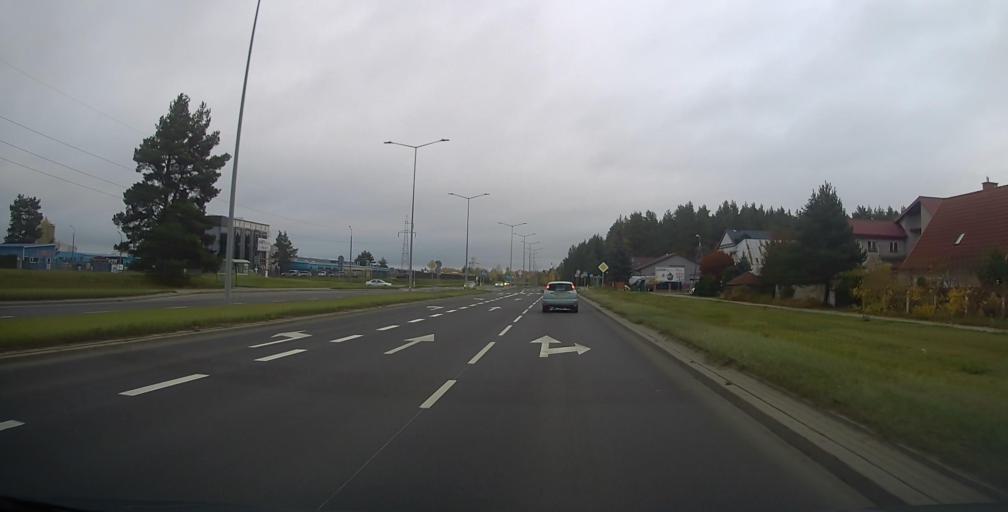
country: PL
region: Warmian-Masurian Voivodeship
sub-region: Powiat elcki
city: Elk
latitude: 53.8139
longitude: 22.3826
